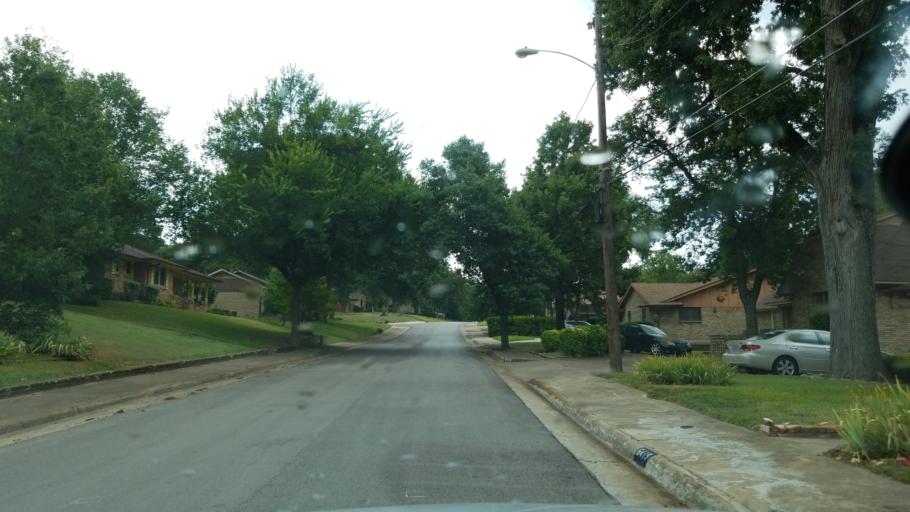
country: US
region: Texas
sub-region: Dallas County
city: Duncanville
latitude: 32.6699
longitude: -96.8370
